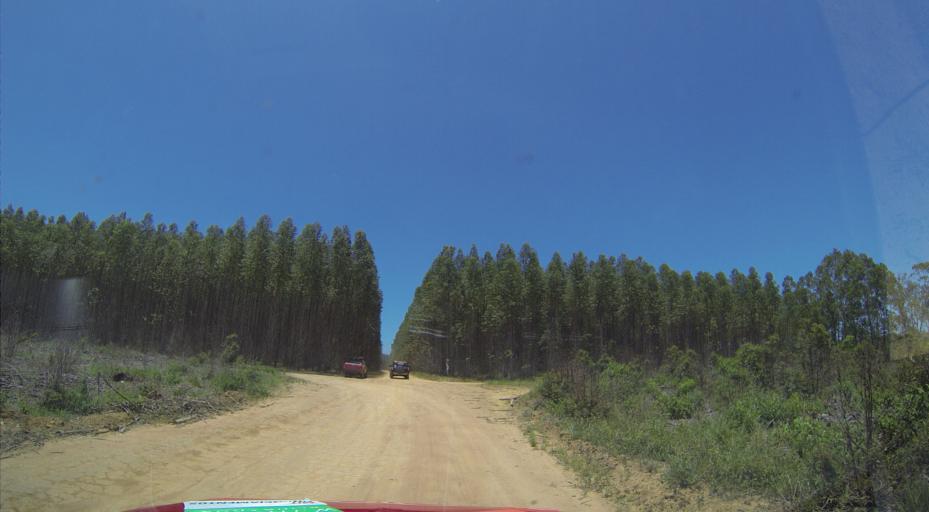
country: BR
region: Espirito Santo
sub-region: Serra
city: Serra
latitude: -19.9875
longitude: -40.2056
